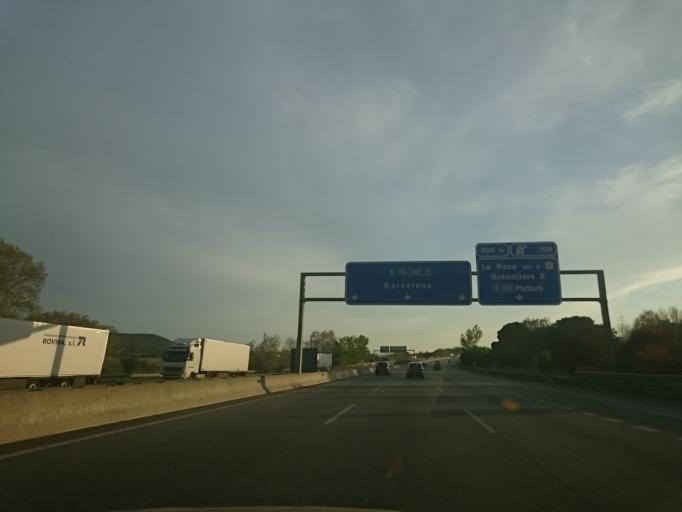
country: ES
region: Catalonia
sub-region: Provincia de Barcelona
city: La Roca del Valles
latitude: 41.6072
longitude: 2.3432
